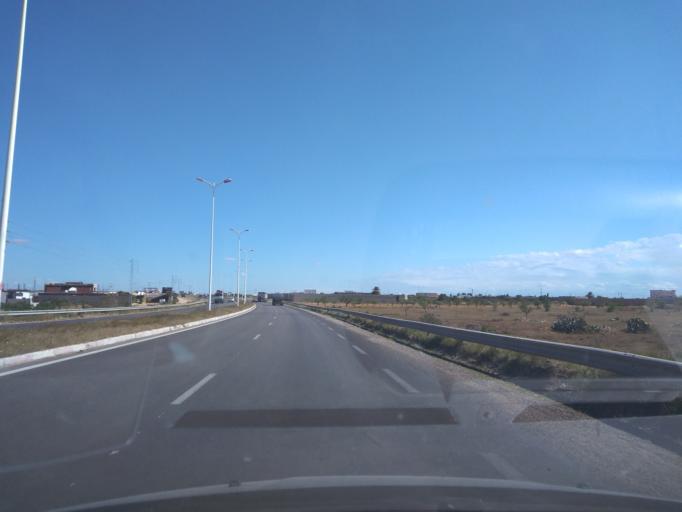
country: TN
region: Safaqis
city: Sfax
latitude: 34.7995
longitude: 10.6848
